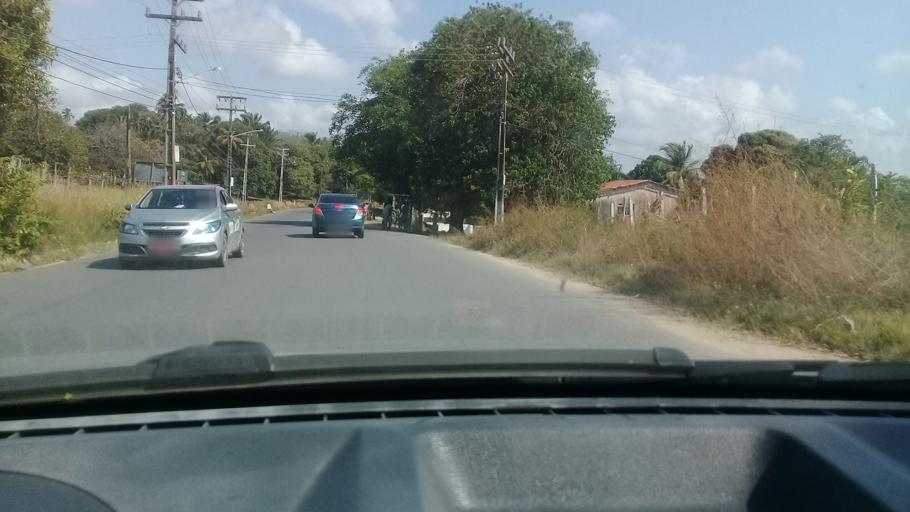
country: BR
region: Pernambuco
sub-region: Itamaraca
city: Itamaraca
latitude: -7.7762
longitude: -34.8360
